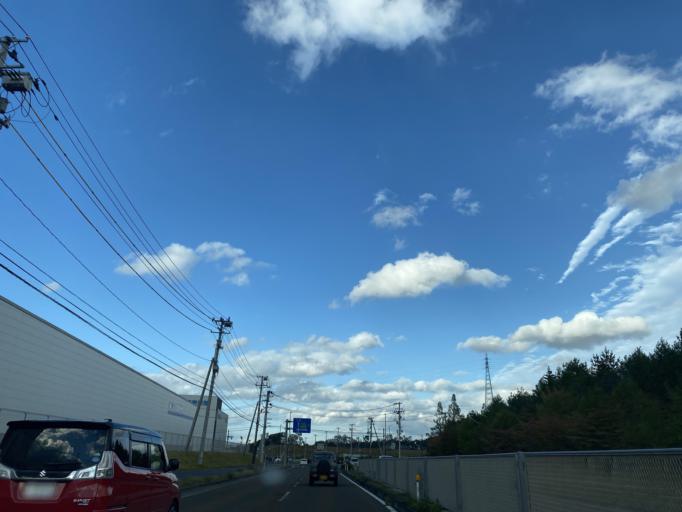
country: JP
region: Miyagi
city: Tomiya
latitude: 38.3683
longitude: 140.8540
